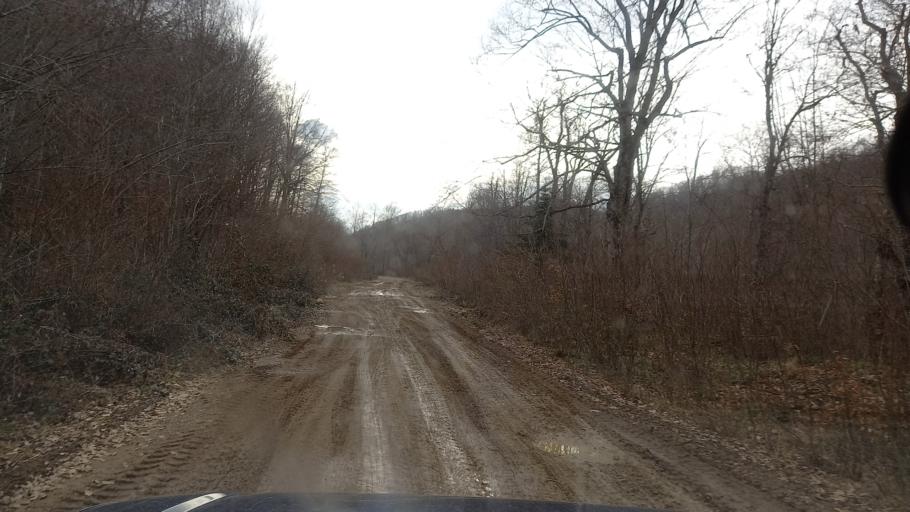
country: RU
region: Adygeya
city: Kamennomostskiy
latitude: 44.1709
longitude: 40.2983
